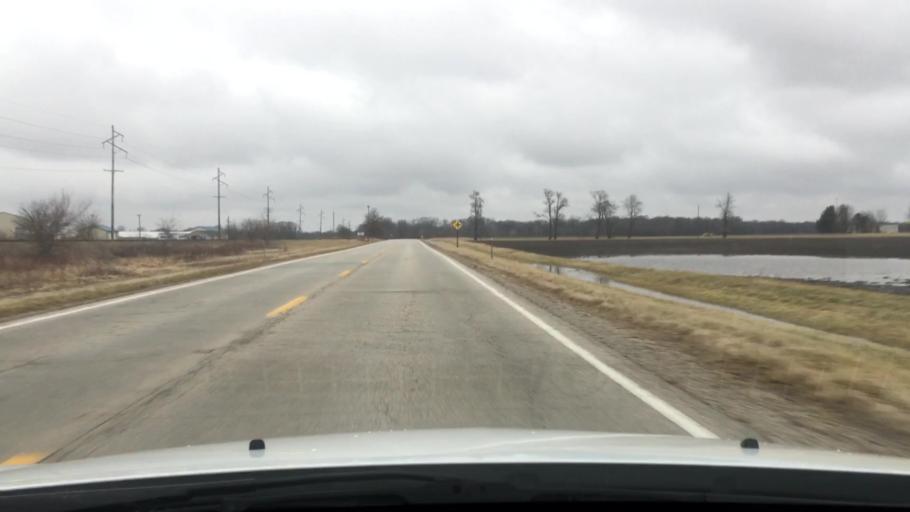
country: US
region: Illinois
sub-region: Iroquois County
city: Sheldon
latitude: 40.8070
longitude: -87.5747
